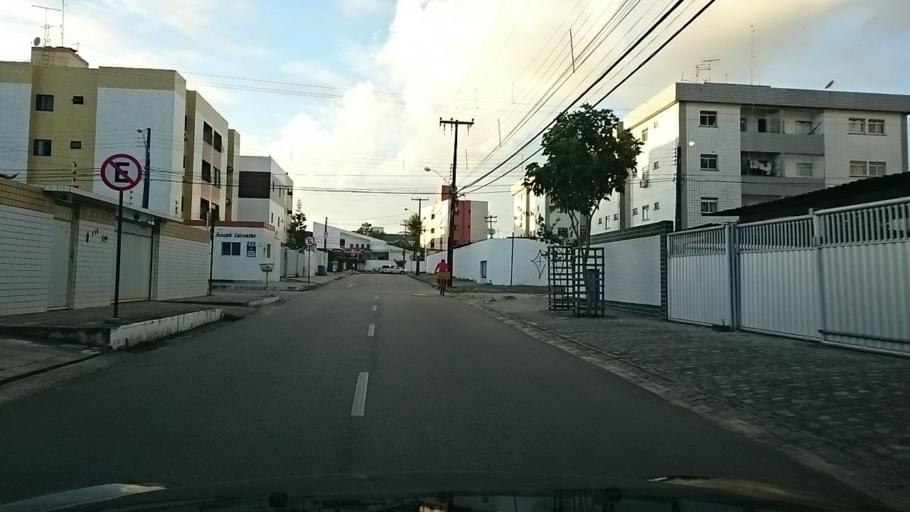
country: BR
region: Paraiba
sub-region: Joao Pessoa
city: Joao Pessoa
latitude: -7.1544
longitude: -34.8359
